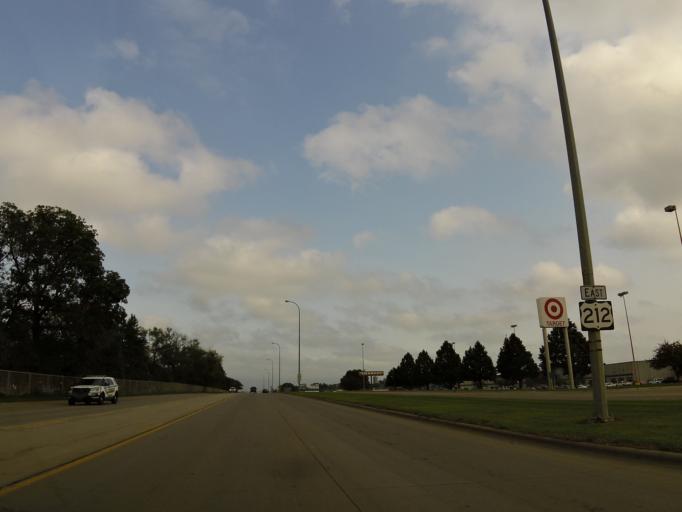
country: US
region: South Dakota
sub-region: Codington County
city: Watertown
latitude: 44.8901
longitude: -97.0851
